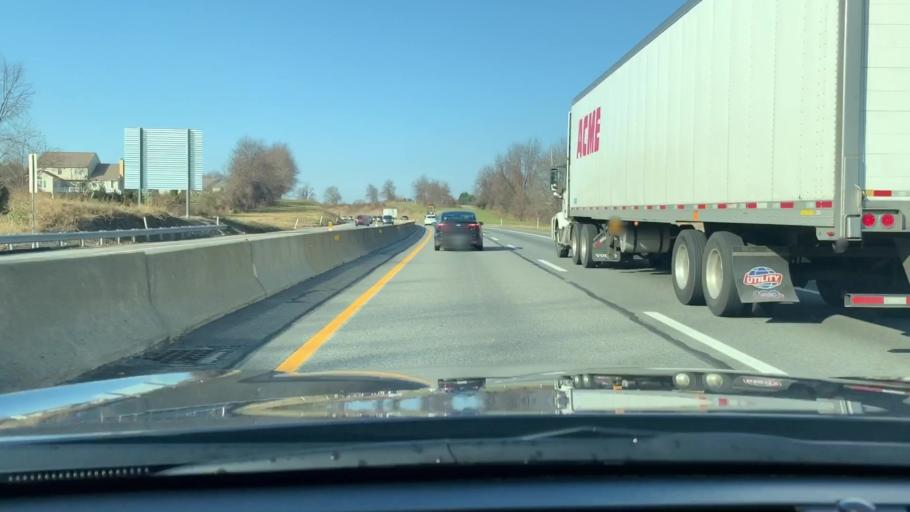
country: US
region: Pennsylvania
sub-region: Chester County
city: Downingtown
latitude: 40.0818
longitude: -75.7075
